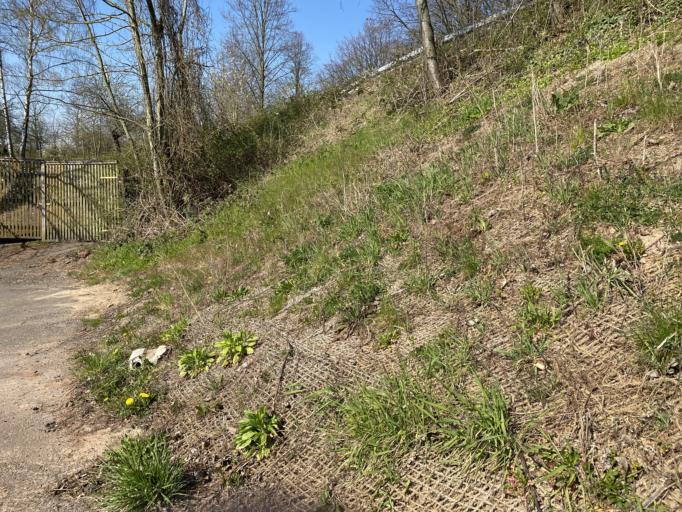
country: DE
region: Hesse
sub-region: Regierungsbezirk Darmstadt
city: Langenselbold
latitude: 50.2300
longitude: 9.0649
